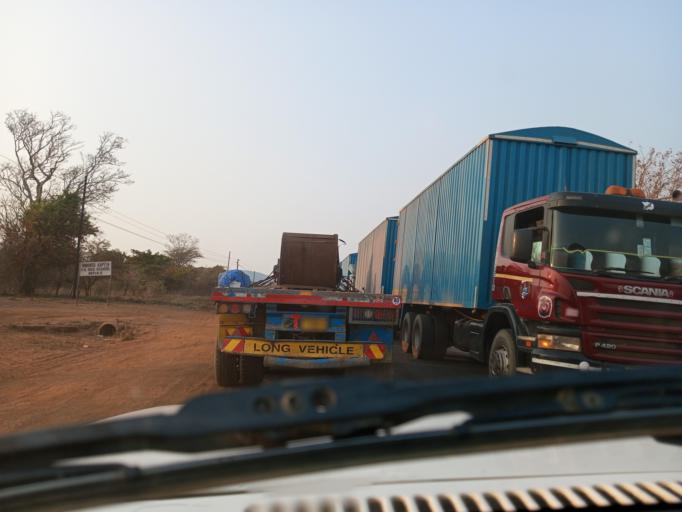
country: ZM
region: Northern
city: Mpika
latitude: -11.9186
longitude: 31.4164
